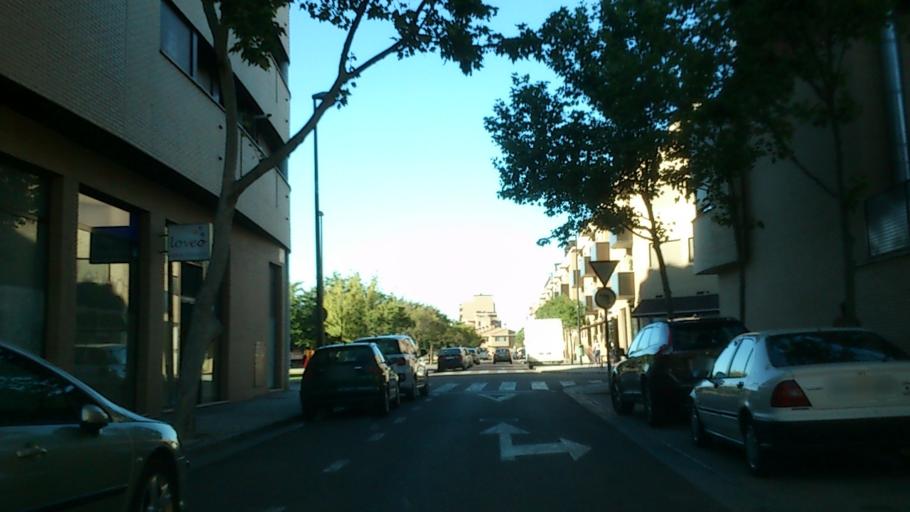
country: ES
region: Aragon
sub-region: Provincia de Zaragoza
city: Zaragoza
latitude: 41.6686
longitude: -0.8336
